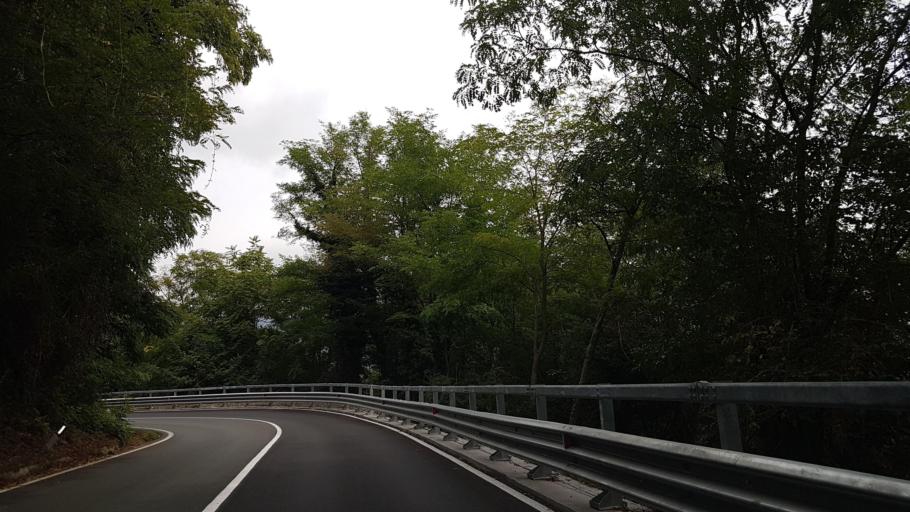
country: IT
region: Liguria
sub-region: Provincia di Genova
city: Moneglia
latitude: 44.2567
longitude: 9.4733
